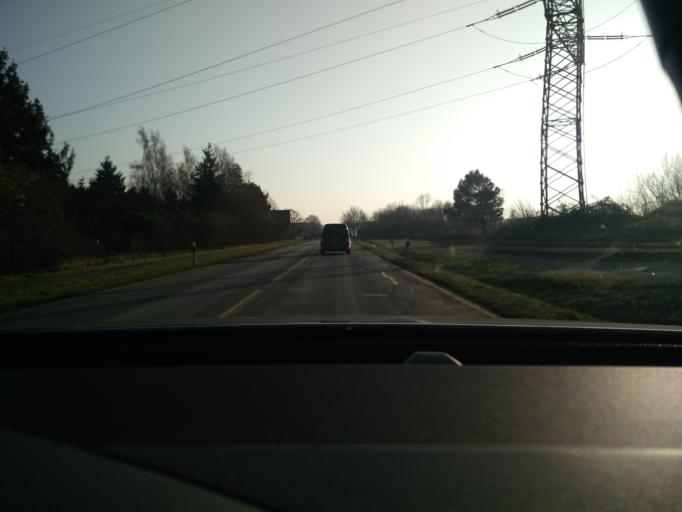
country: DE
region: Lower Saxony
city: Ilsede
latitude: 52.2998
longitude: 10.2055
